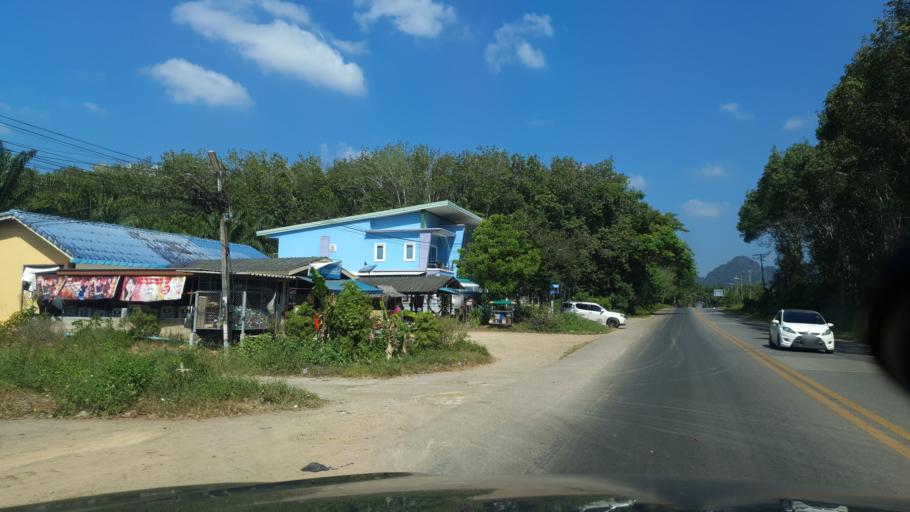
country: TH
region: Krabi
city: Krabi
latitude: 8.0645
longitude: 98.8594
